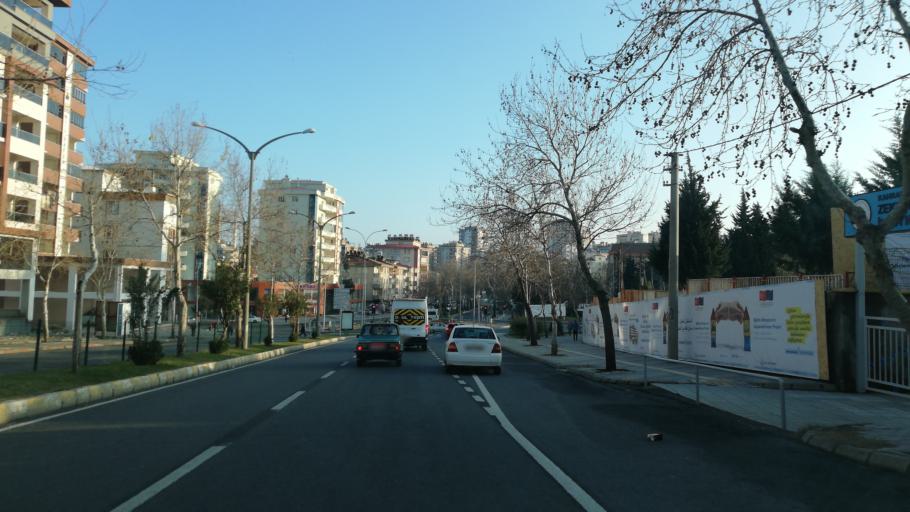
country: TR
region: Kahramanmaras
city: Kahramanmaras
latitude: 37.5877
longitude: 36.9036
